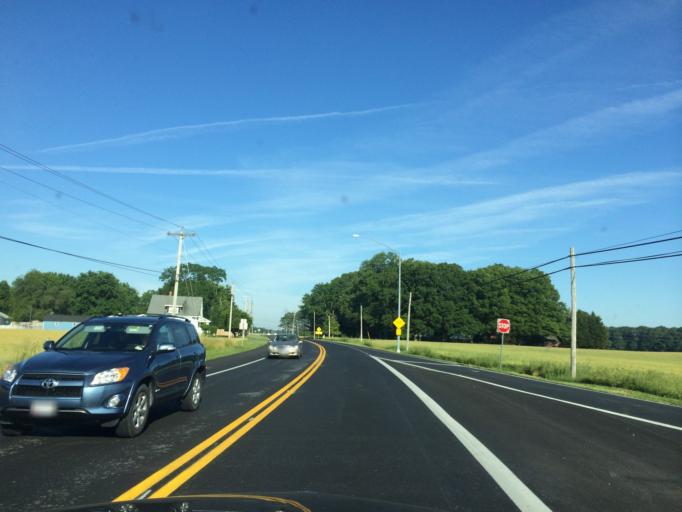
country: US
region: Maryland
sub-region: Wicomico County
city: Salisbury
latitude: 38.3714
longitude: -75.6301
